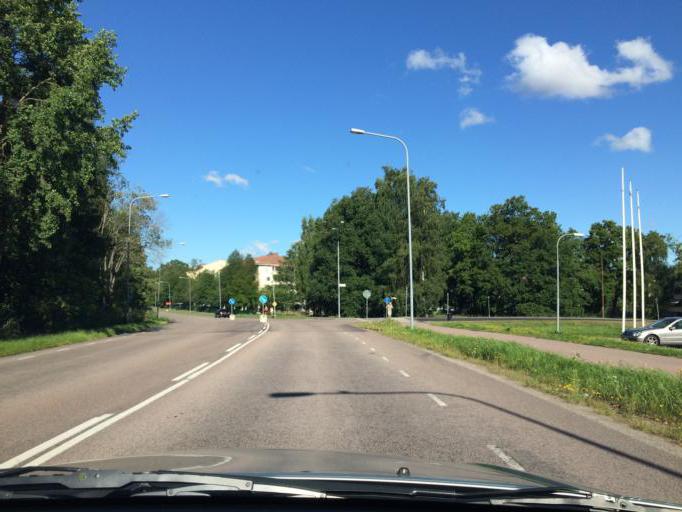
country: SE
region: Vaestmanland
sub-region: Vasteras
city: Vasteras
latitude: 59.6052
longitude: 16.5832
